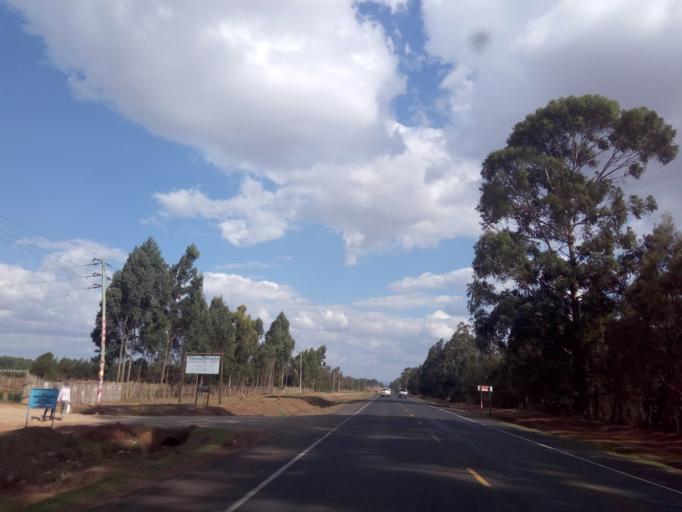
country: KE
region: Uasin Gishu
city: Eldoret
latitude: 0.4188
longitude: 35.3171
